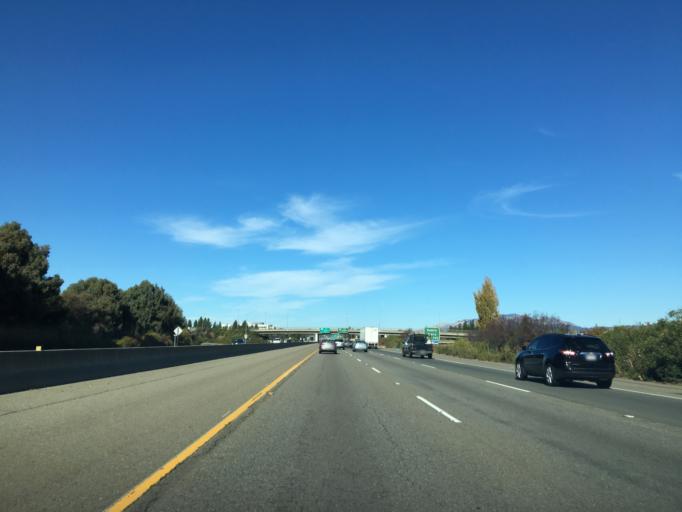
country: US
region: California
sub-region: Alameda County
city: Dublin
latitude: 37.6874
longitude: -121.9173
